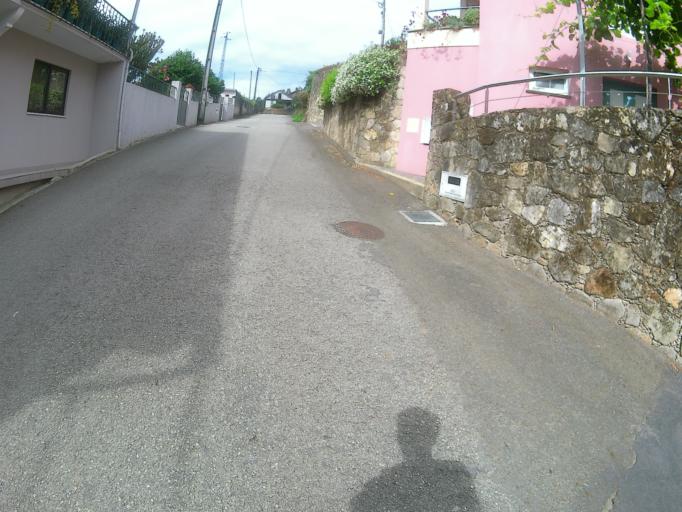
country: PT
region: Aveiro
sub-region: Albergaria-A-Velha
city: Branca
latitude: 40.7576
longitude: -8.4241
